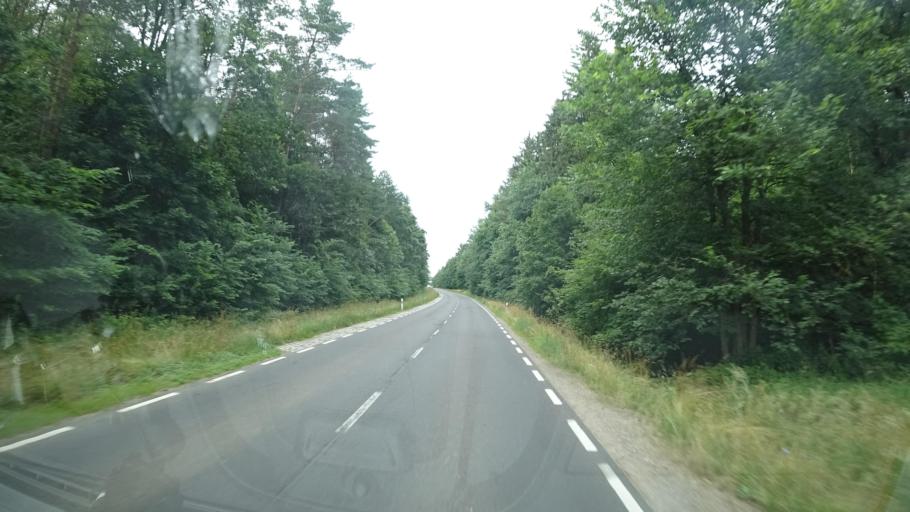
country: PL
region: Warmian-Masurian Voivodeship
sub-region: Powiat goldapski
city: Goldap
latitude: 54.3269
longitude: 22.2978
